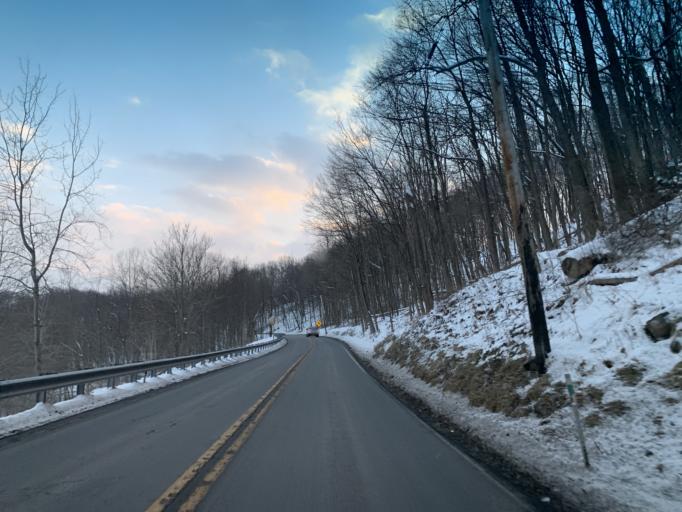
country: US
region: Maryland
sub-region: Allegany County
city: Frostburg
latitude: 39.6911
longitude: -78.8870
